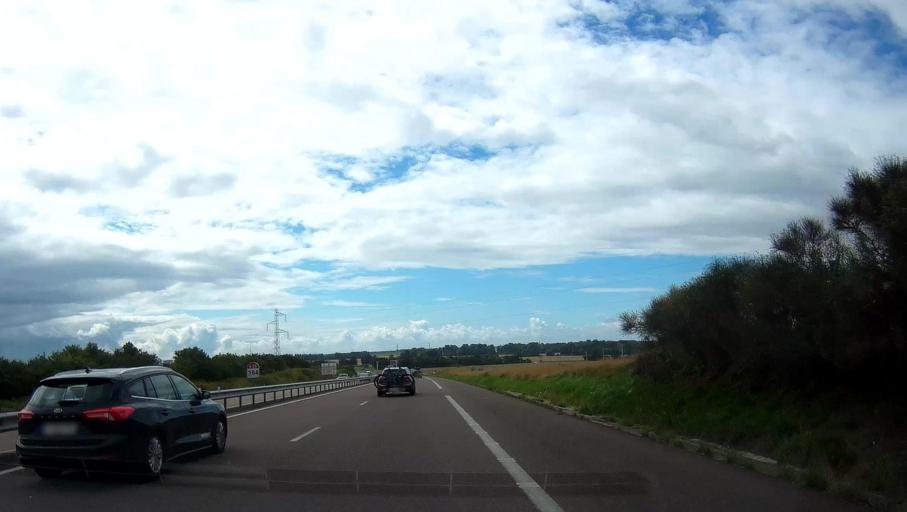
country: FR
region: Champagne-Ardenne
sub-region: Departement de l'Aube
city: Creney-pres-Troyes
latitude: 48.3195
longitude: 4.1646
